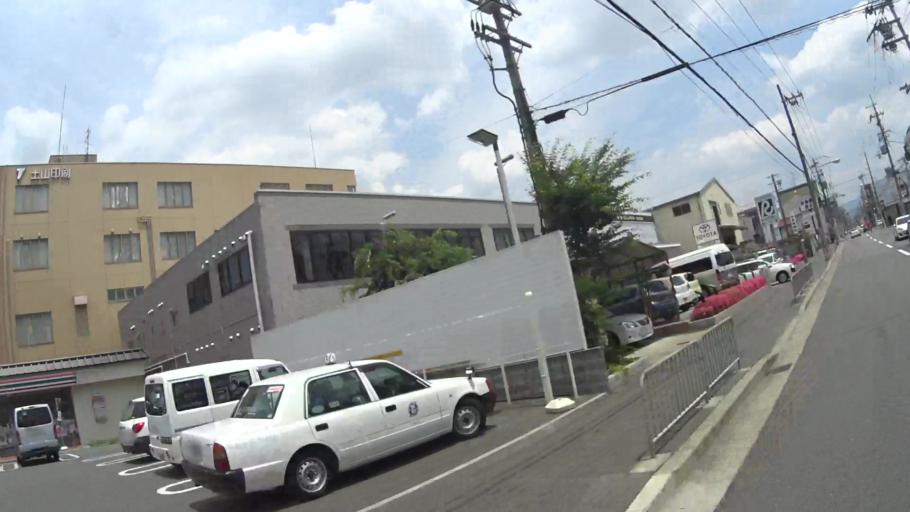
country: JP
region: Kyoto
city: Muko
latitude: 34.9841
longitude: 135.7245
